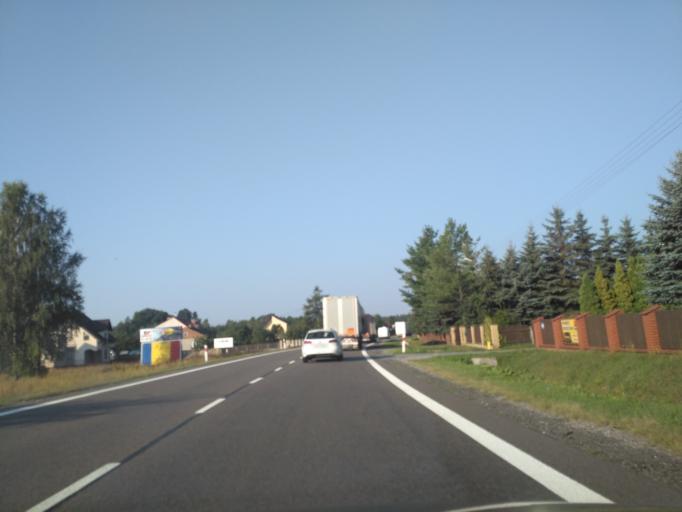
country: PL
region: Lublin Voivodeship
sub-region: Powiat janowski
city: Janow Lubelski
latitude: 50.6961
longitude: 22.3857
